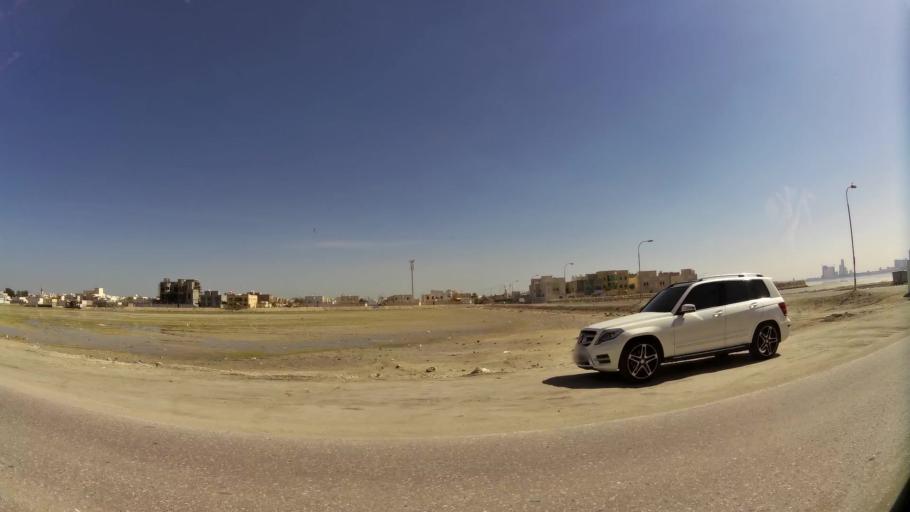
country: BH
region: Muharraq
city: Al Hadd
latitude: 26.2440
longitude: 50.6337
